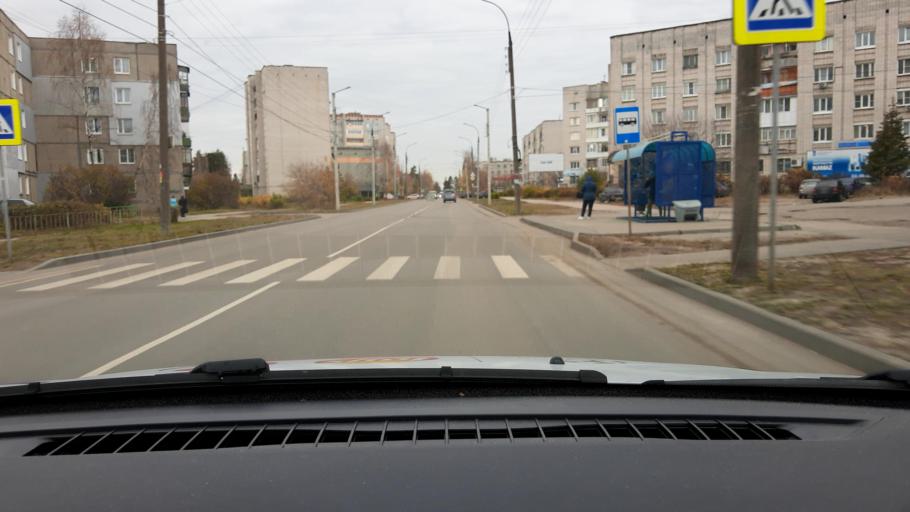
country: RU
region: Nizjnij Novgorod
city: Dzerzhinsk
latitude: 56.2555
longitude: 43.4528
